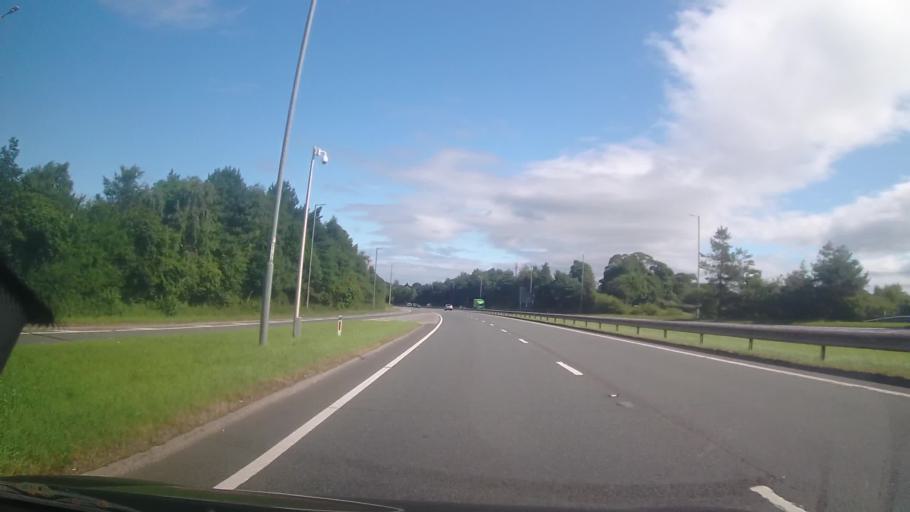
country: GB
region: Wales
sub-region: Wrexham
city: Gresford
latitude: 53.0759
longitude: -2.9872
